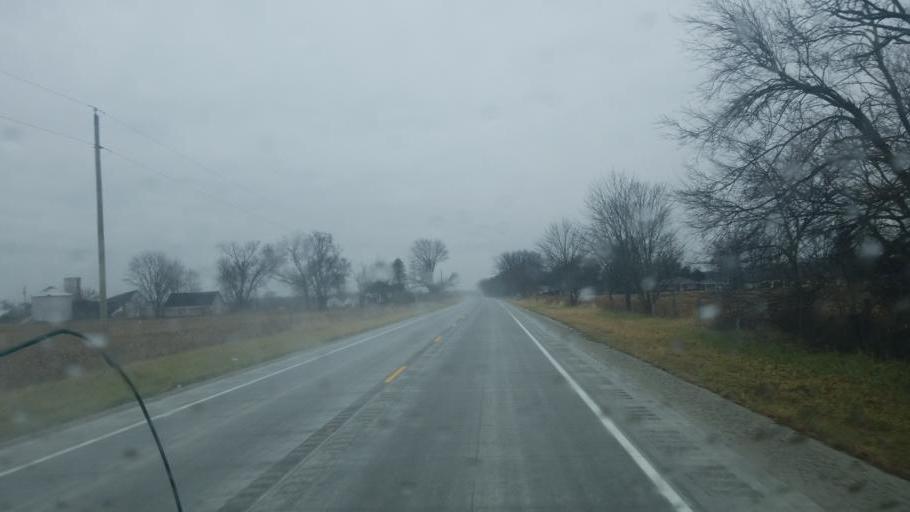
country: US
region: Indiana
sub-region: Shelby County
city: Shelbyville
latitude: 39.4623
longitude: -85.7616
